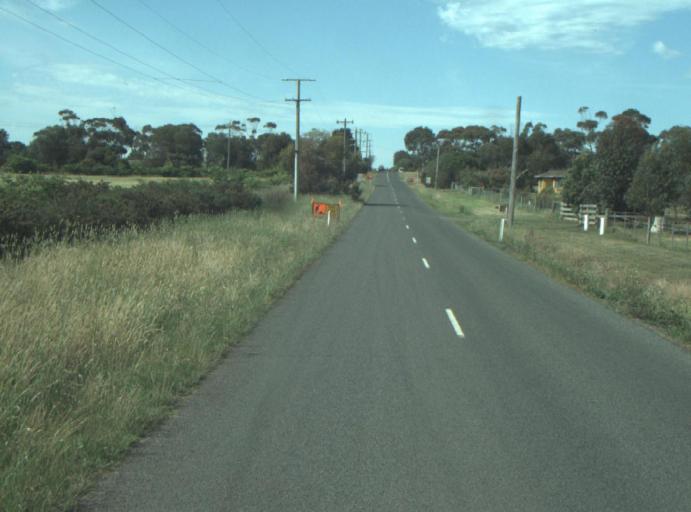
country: AU
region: Victoria
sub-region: Greater Geelong
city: Clifton Springs
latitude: -38.1682
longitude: 144.5155
